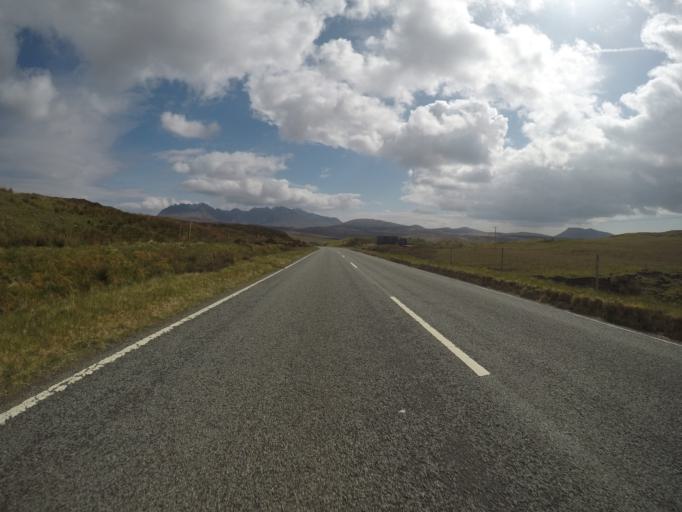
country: GB
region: Scotland
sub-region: Highland
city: Isle of Skye
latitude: 57.3096
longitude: -6.3178
